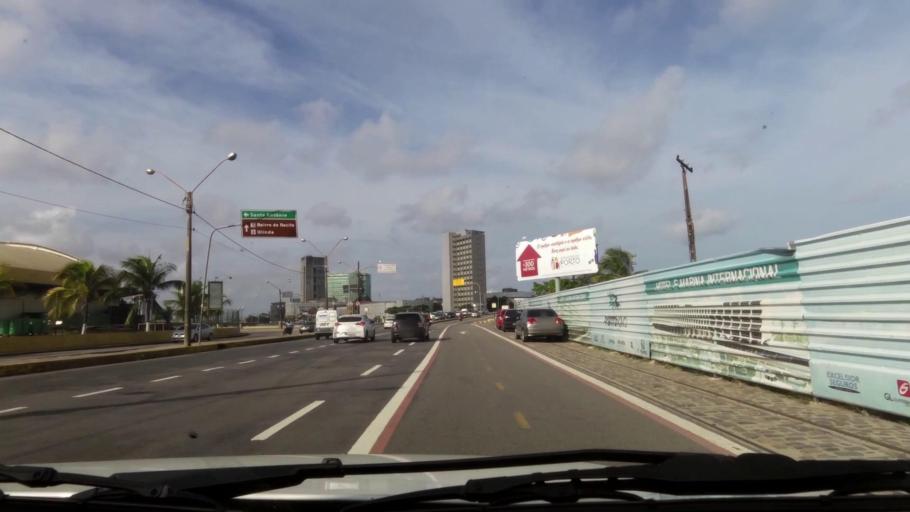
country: BR
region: Pernambuco
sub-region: Recife
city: Recife
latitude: -8.0685
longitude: -34.8747
